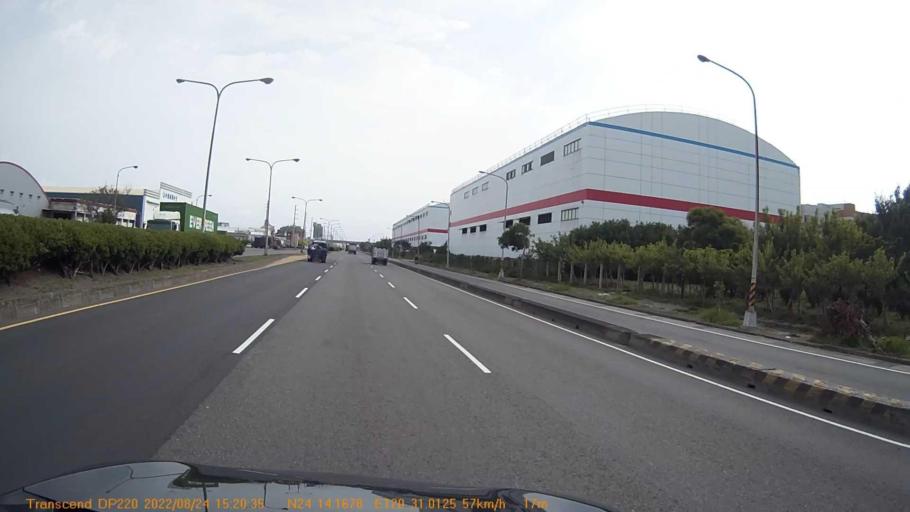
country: TW
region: Taiwan
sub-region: Changhua
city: Chang-hua
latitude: 24.2357
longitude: 120.5167
